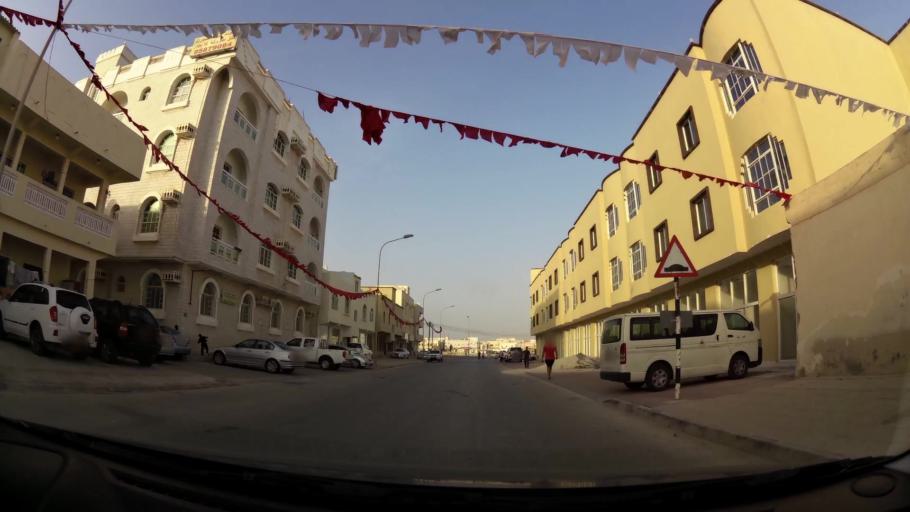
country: OM
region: Zufar
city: Salalah
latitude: 17.0142
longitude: 54.0987
